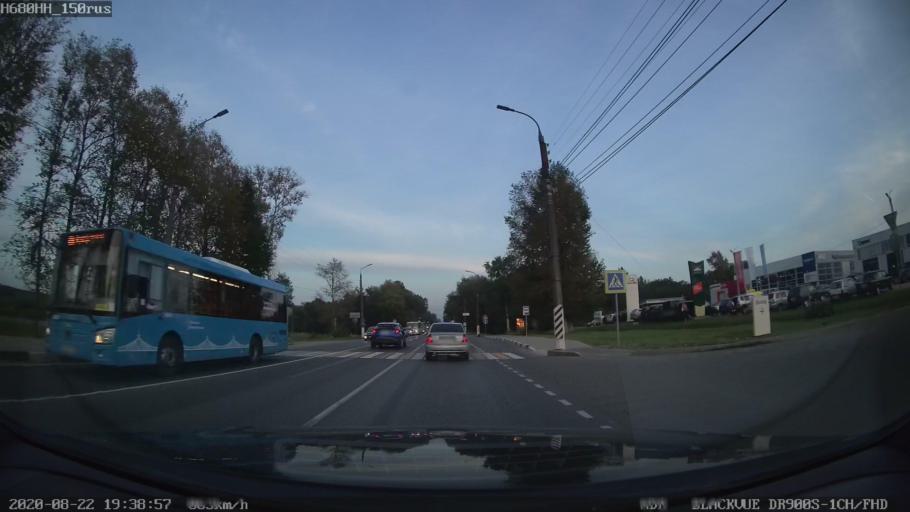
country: RU
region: Tverskaya
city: Sakharovo
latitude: 56.8098
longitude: 36.0056
